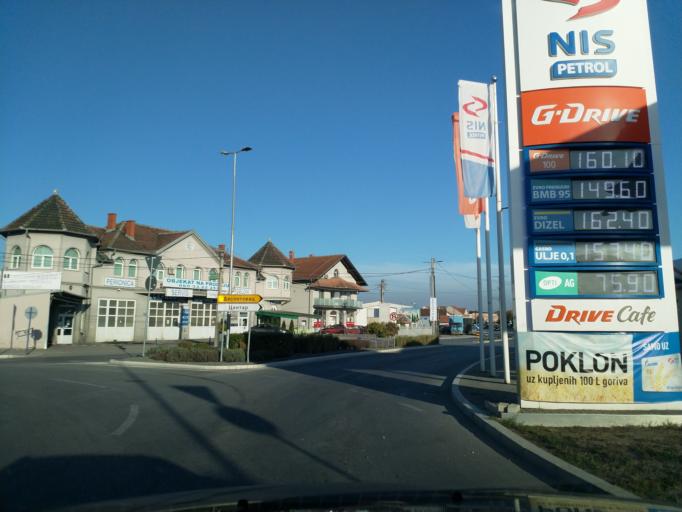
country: RS
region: Central Serbia
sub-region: Pomoravski Okrug
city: Svilajnac
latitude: 44.2331
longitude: 21.1861
